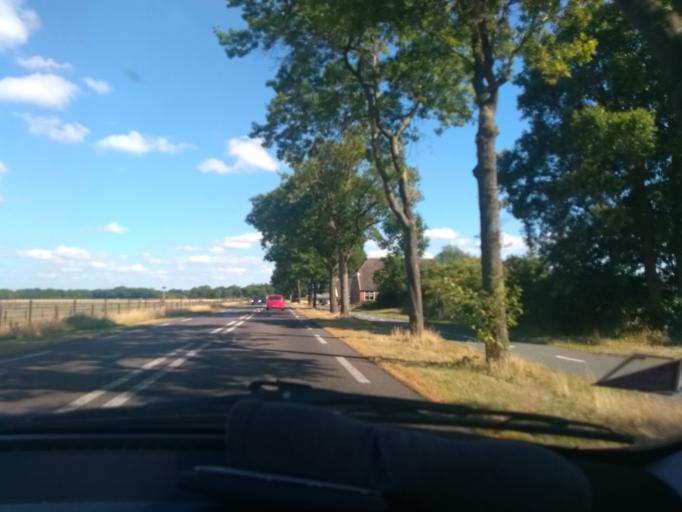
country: NL
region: Drenthe
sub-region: Gemeente Tynaarlo
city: Vries
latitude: 53.0871
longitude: 6.5616
